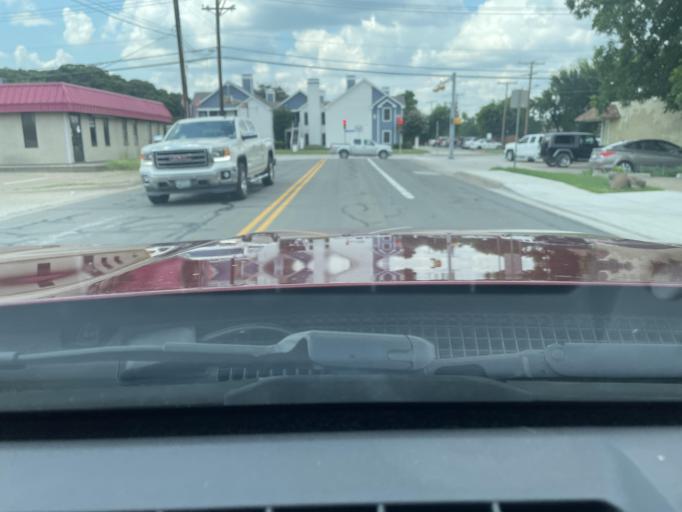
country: US
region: Texas
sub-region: Tarrant County
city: Dalworthington Gardens
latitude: 32.7061
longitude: -97.1279
